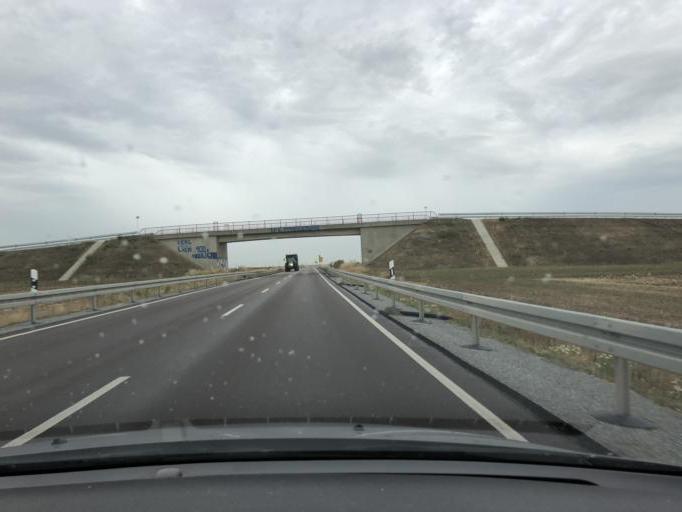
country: DE
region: Saxony-Anhalt
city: Brumby
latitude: 51.8908
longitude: 11.7057
